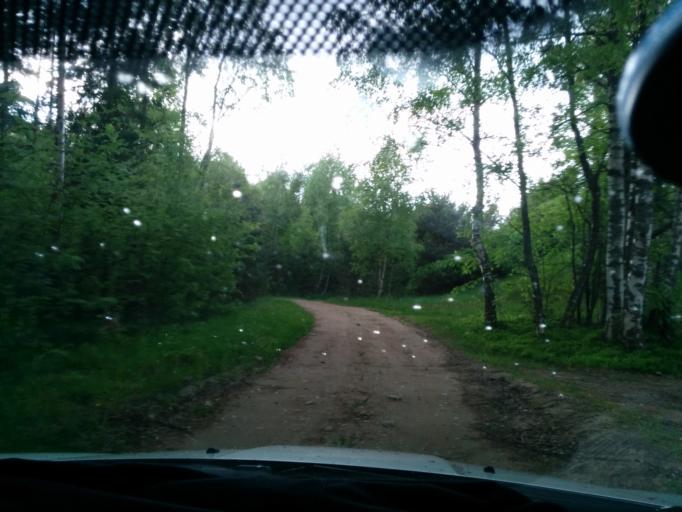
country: EE
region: Harju
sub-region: Loksa linn
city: Loksa
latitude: 59.6662
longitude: 25.7033
